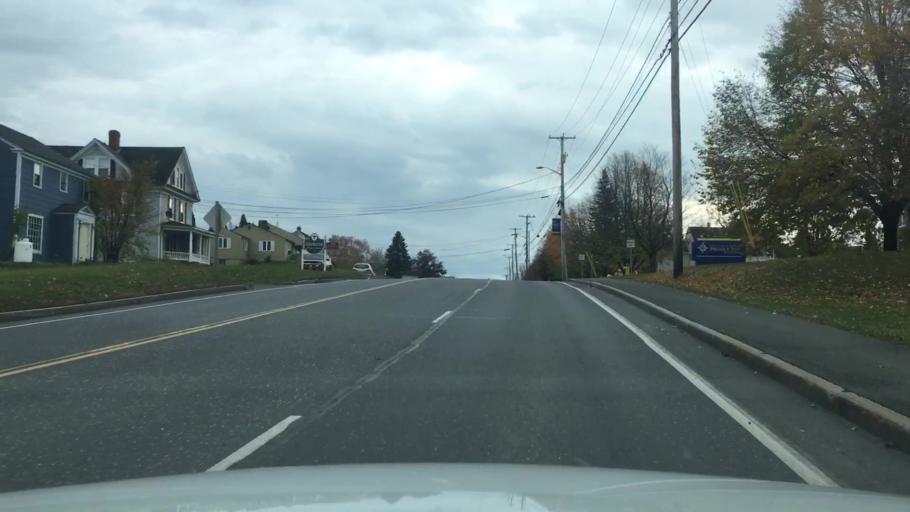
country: US
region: Maine
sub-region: Aroostook County
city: Presque Isle
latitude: 46.6731
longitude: -68.0156
